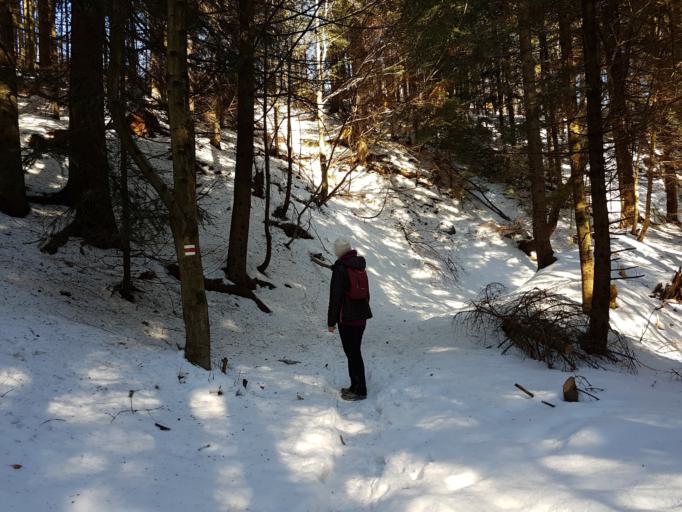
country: SK
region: Banskobystricky
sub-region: Okres Banska Bystrica
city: Banska Bystrica
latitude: 48.8156
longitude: 19.1447
